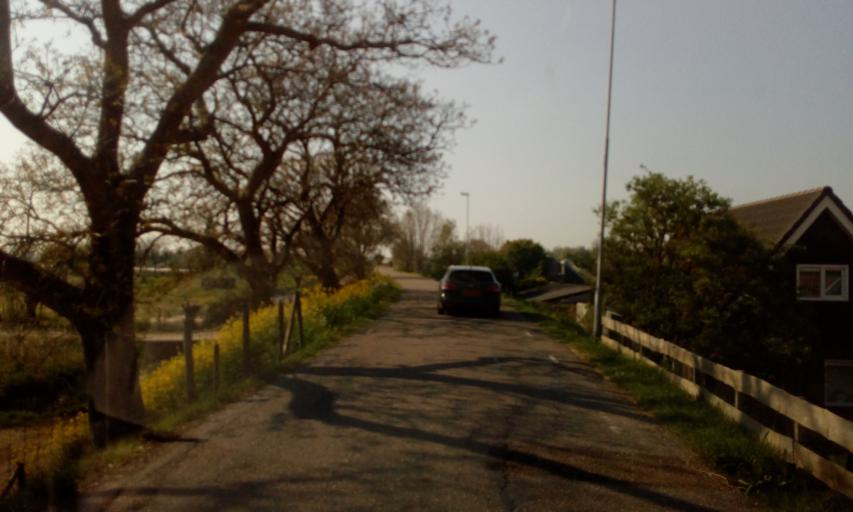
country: NL
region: South Holland
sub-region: Gemeente Zwijndrecht
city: Heerjansdam
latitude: 51.8205
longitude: 4.5742
